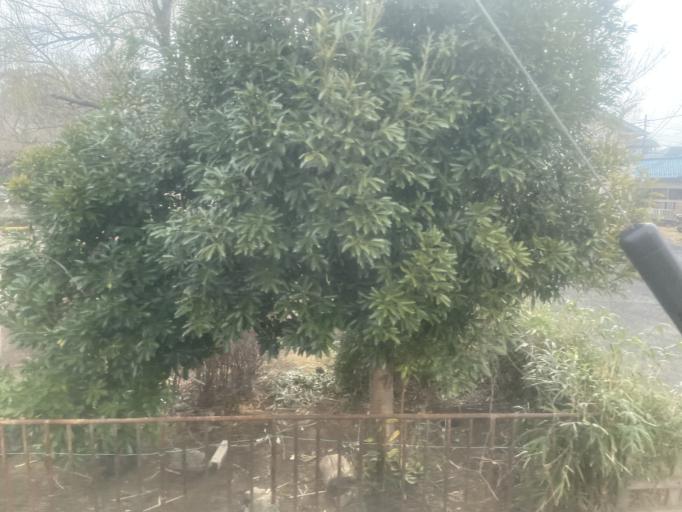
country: JP
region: Tokyo
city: Higashimurayama-shi
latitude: 35.7712
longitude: 139.4711
